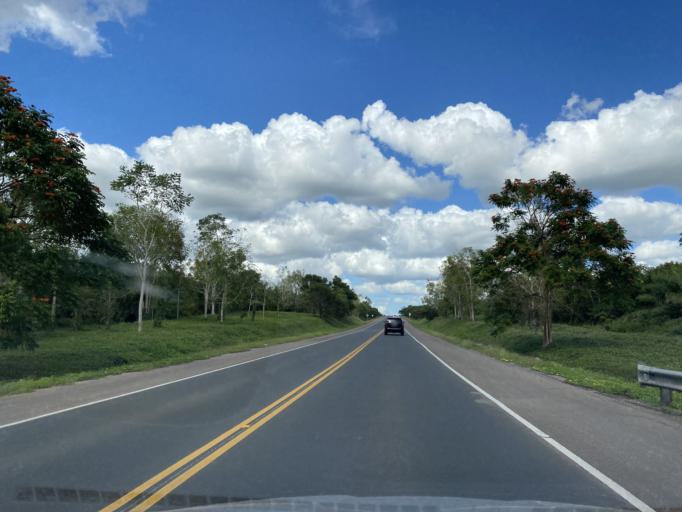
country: DO
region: Monte Plata
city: Monte Plata
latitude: 18.7227
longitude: -69.7605
